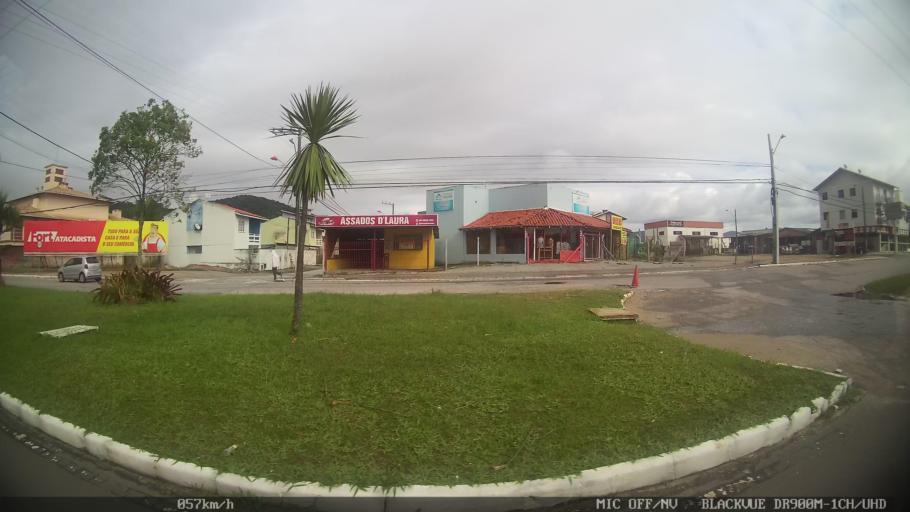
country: BR
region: Santa Catarina
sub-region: Sao Jose
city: Campinas
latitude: -27.5672
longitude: -48.6325
